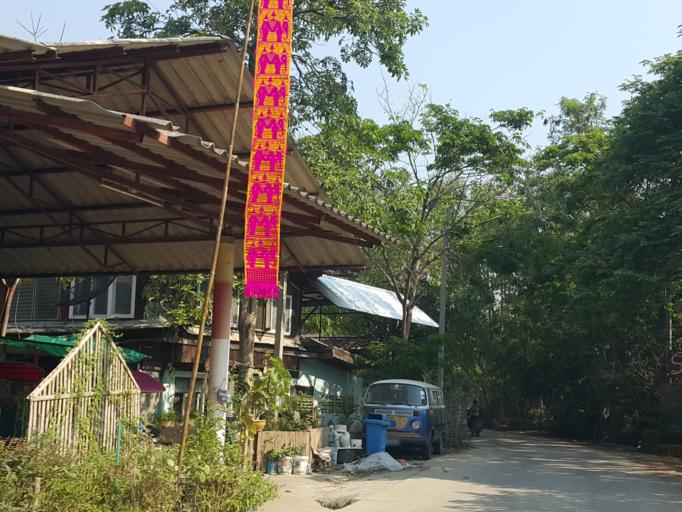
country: TH
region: Chiang Mai
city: San Kamphaeng
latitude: 18.7730
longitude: 99.0776
